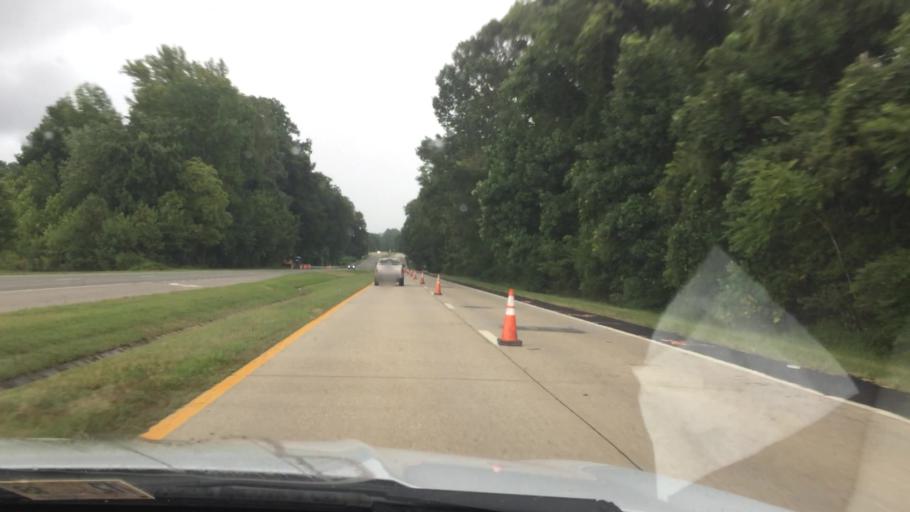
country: US
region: Virginia
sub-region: King William County
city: West Point
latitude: 37.3995
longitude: -76.7987
